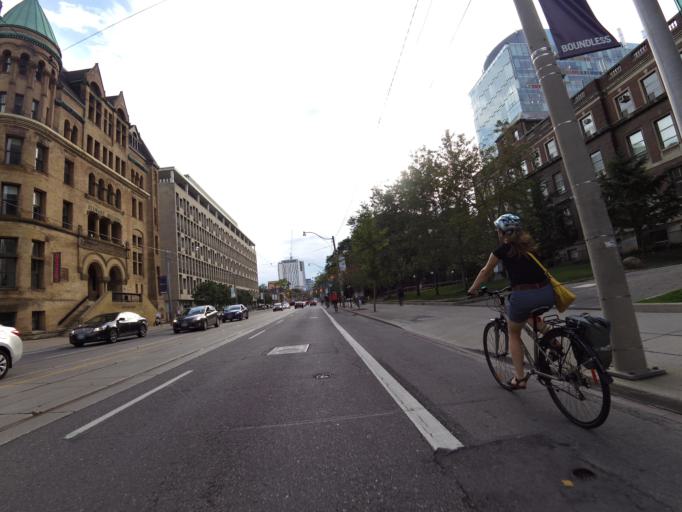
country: CA
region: Ontario
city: Toronto
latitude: 43.6596
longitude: -79.3919
